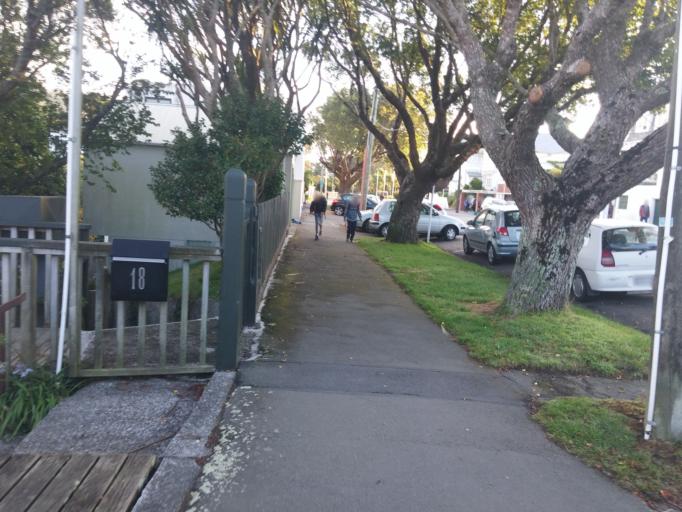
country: NZ
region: Wellington
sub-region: Wellington City
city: Kelburn
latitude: -41.2864
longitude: 174.7663
